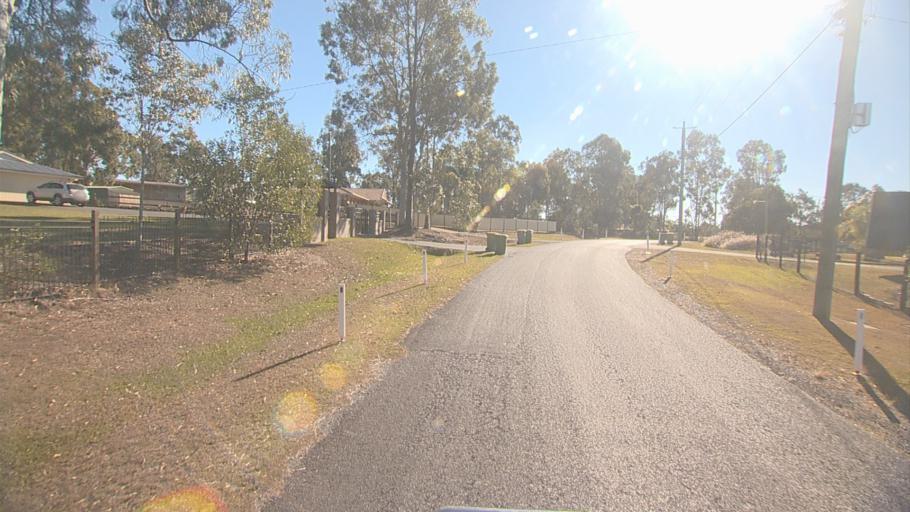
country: AU
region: Queensland
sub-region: Logan
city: North Maclean
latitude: -27.7383
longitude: 152.9641
